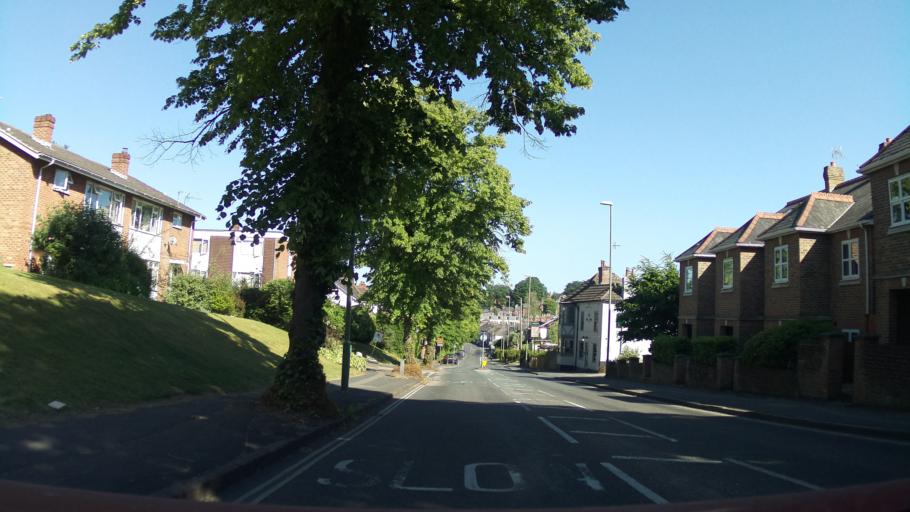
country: GB
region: England
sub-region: Hampshire
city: Winchester
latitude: 51.0690
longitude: -1.3283
